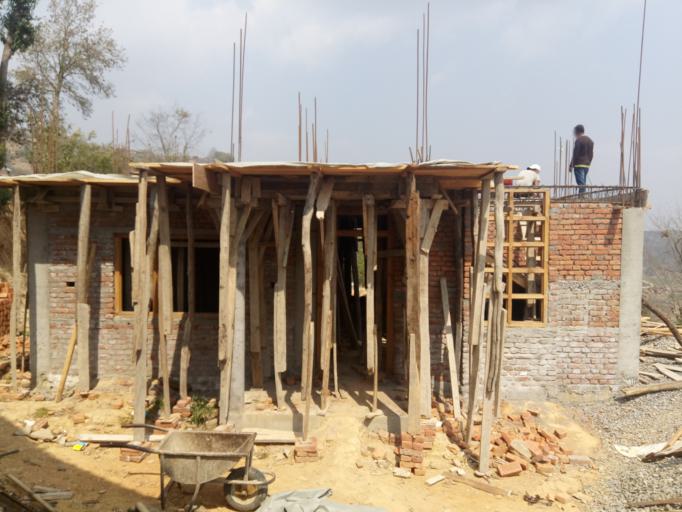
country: NP
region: Central Region
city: Kirtipur
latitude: 27.5959
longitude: 85.2646
